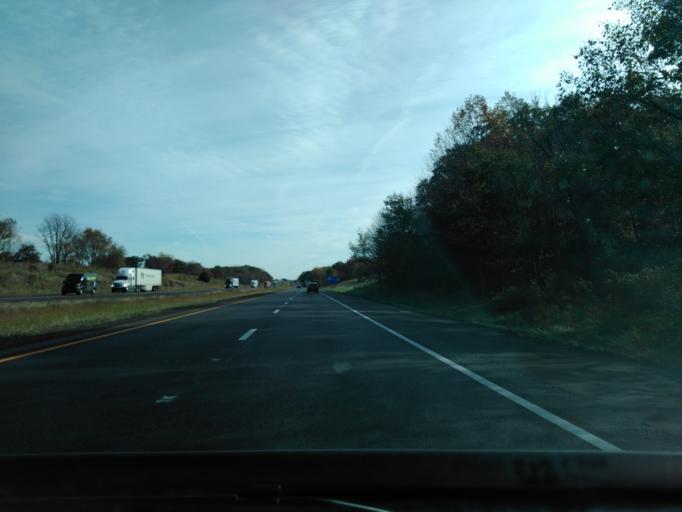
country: US
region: Illinois
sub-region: Madison County
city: Highland
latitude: 38.7864
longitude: -89.6645
